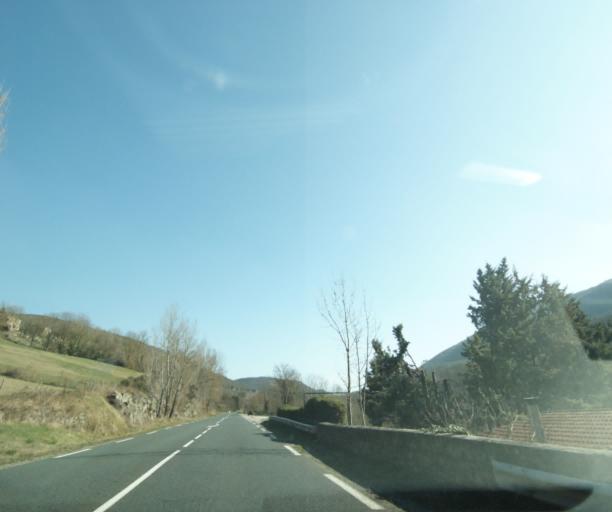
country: FR
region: Midi-Pyrenees
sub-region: Departement de l'Aveyron
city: Saint-Affrique
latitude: 43.9509
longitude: 2.9157
